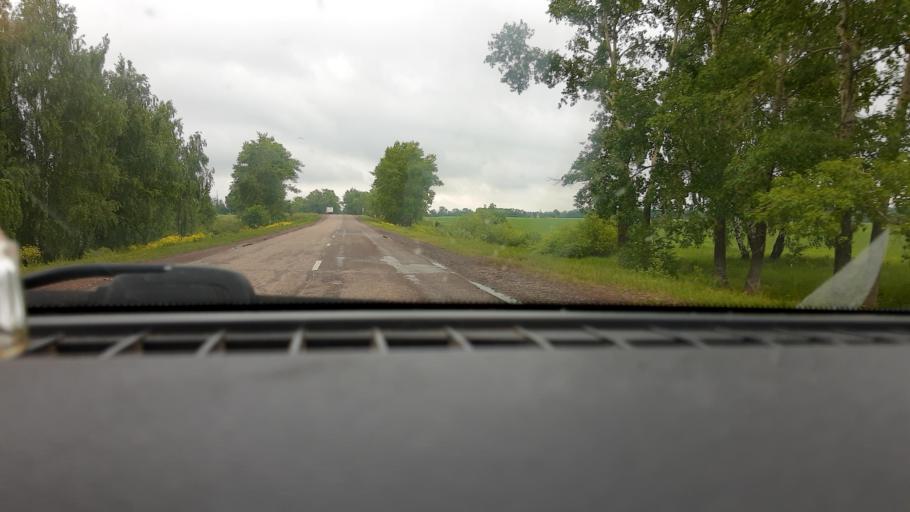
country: RU
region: Bashkortostan
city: Priyutovo
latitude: 53.9320
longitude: 53.9710
